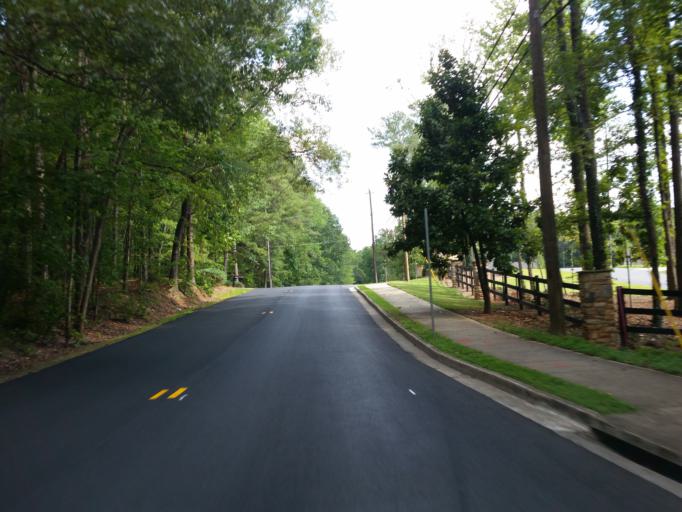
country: US
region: Georgia
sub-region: Cobb County
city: Marietta
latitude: 33.9895
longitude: -84.4603
